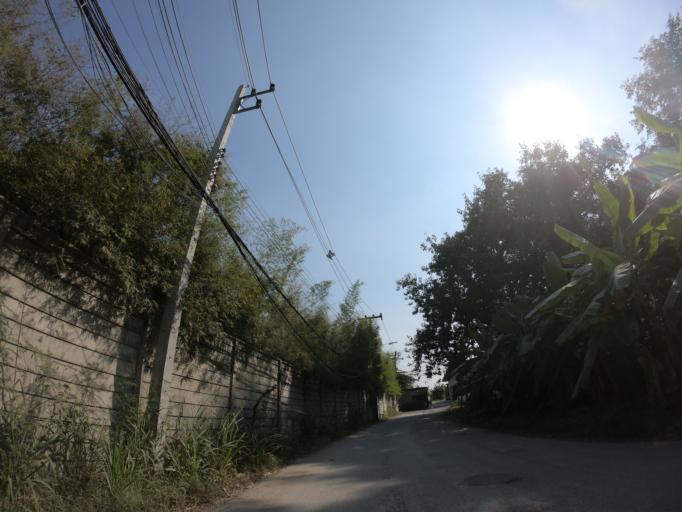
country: TH
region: Chiang Mai
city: Chiang Mai
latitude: 18.8241
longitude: 98.9853
